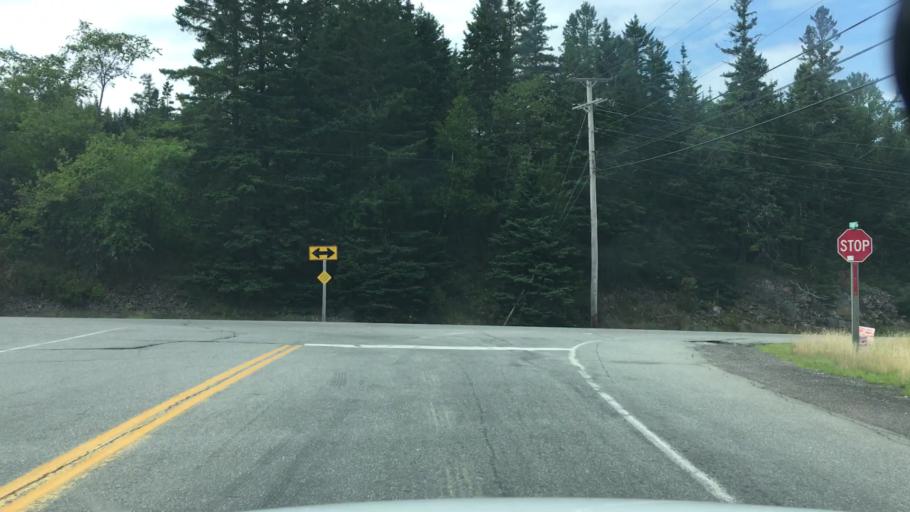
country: CA
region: New Brunswick
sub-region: Charlotte County
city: Saint Andrews
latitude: 44.9704
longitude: -67.0751
